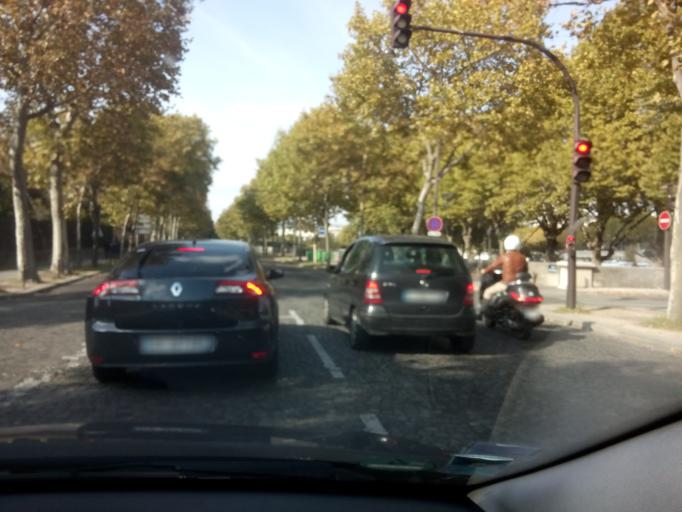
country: FR
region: Ile-de-France
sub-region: Paris
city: Paris
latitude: 48.8447
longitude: 2.3641
